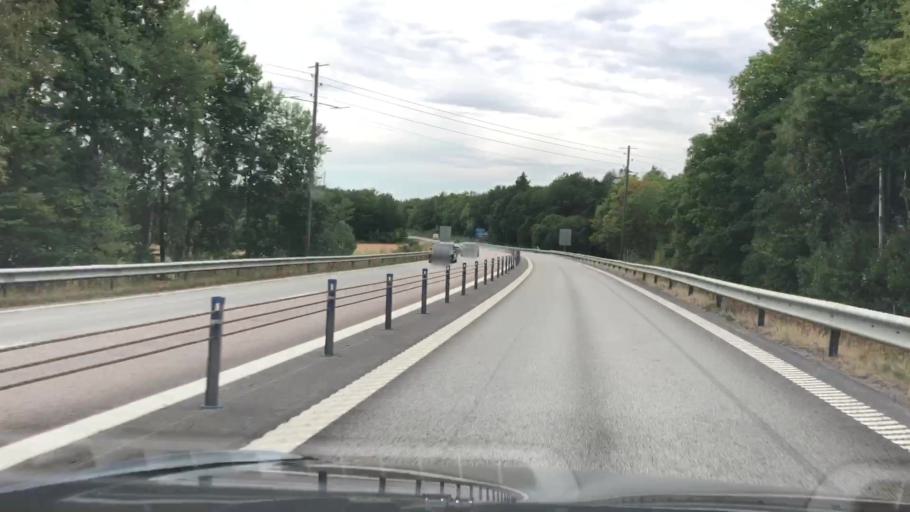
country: SE
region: Blekinge
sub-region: Karlshamns Kommun
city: Morrum
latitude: 56.1896
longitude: 14.7905
